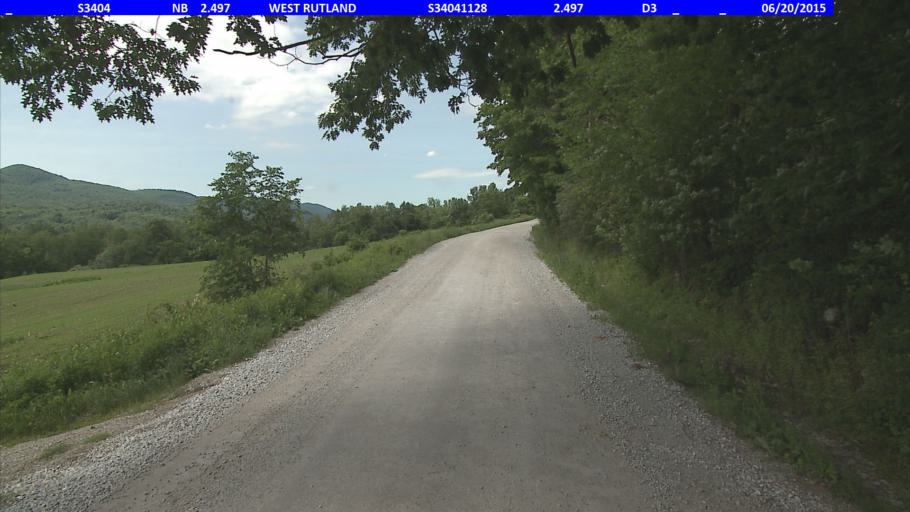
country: US
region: Vermont
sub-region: Rutland County
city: West Rutland
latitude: 43.6265
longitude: -73.0554
